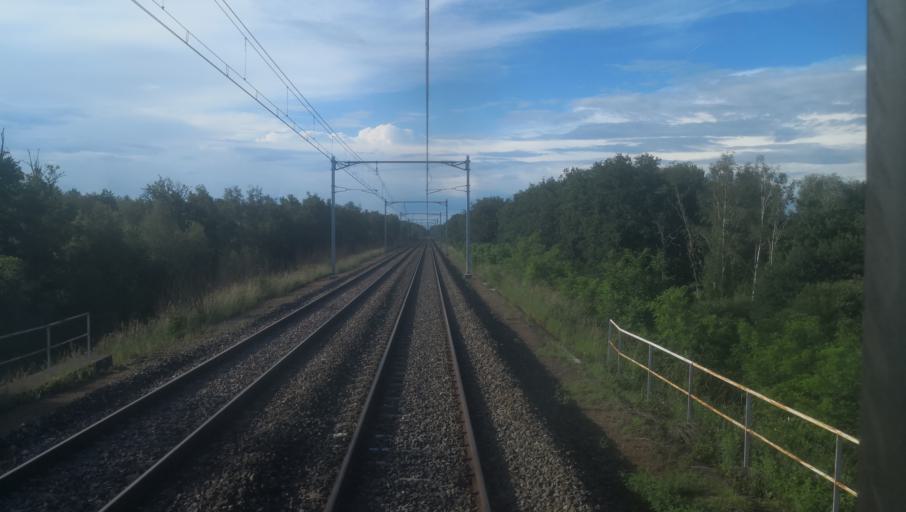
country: FR
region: Centre
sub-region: Departement du Loir-et-Cher
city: Theillay
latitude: 47.3327
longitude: 2.0458
